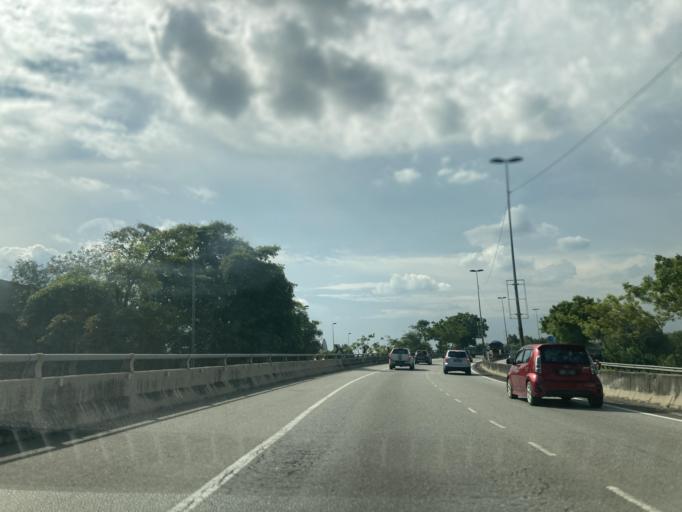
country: MY
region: Selangor
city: Kampung Baru Subang
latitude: 3.1351
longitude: 101.5532
